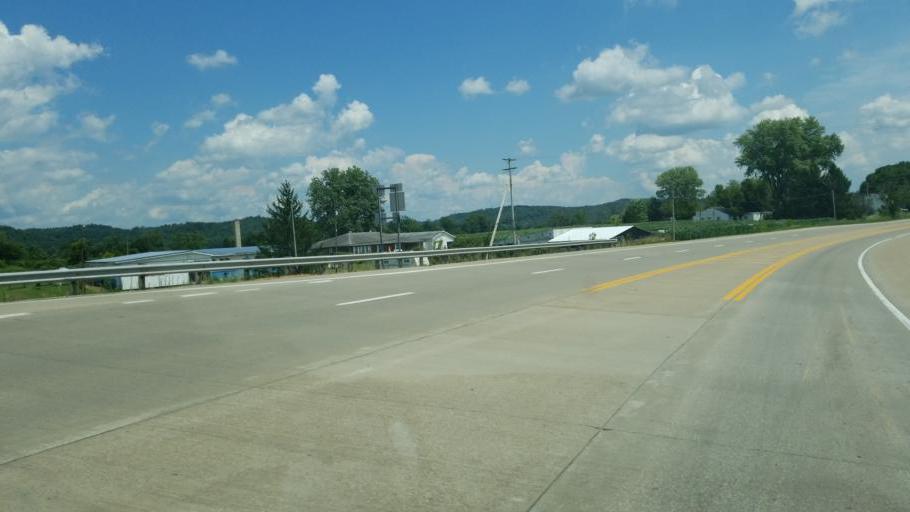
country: US
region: West Virginia
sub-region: Putnam County
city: Buffalo
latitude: 38.7665
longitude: -82.0070
